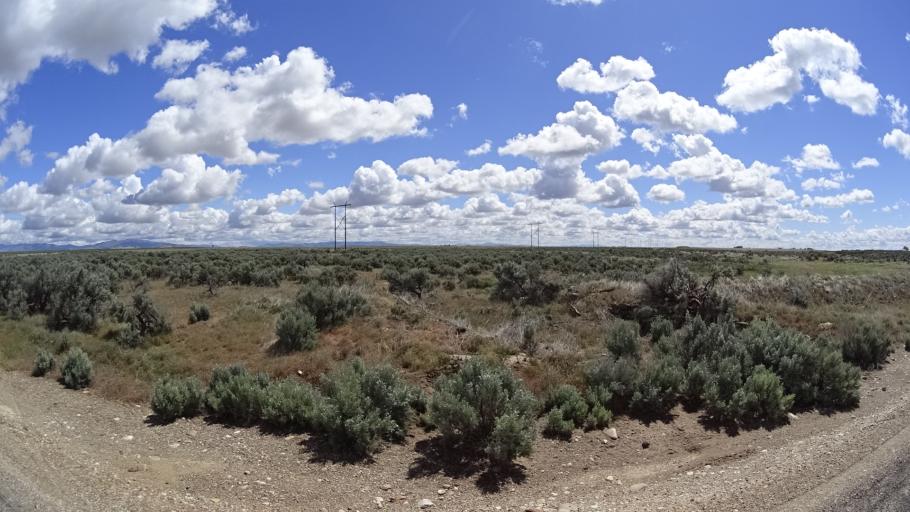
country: US
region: Idaho
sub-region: Ada County
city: Kuna
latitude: 43.4751
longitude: -116.2743
